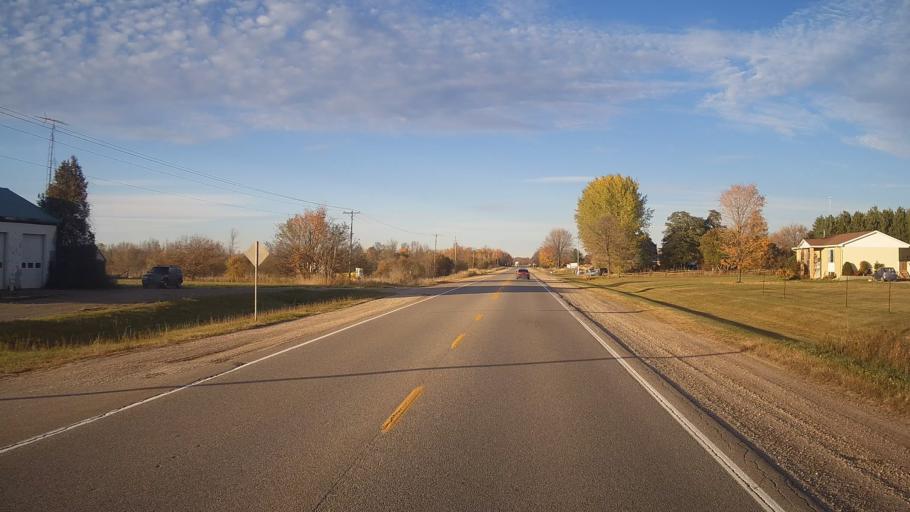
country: CA
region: Ontario
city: Perth
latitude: 44.9646
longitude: -76.2309
